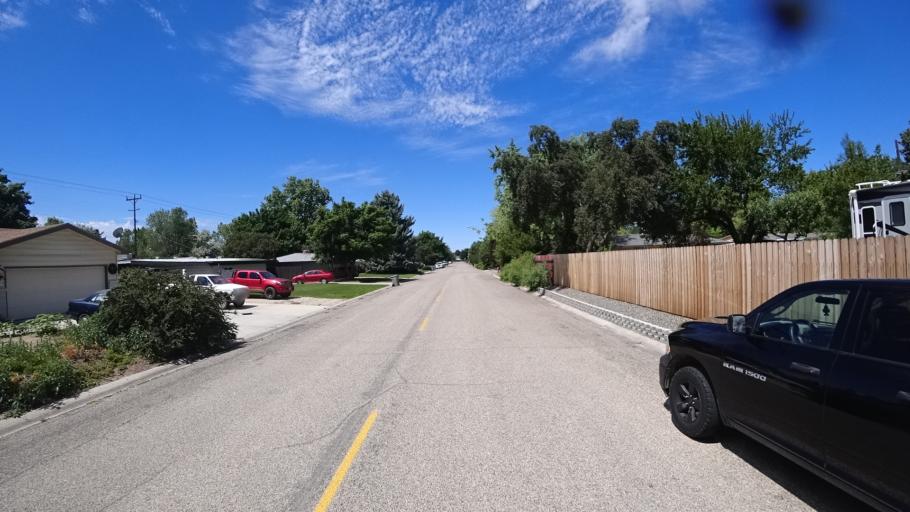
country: US
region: Idaho
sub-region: Ada County
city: Boise
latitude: 43.5756
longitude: -116.2293
